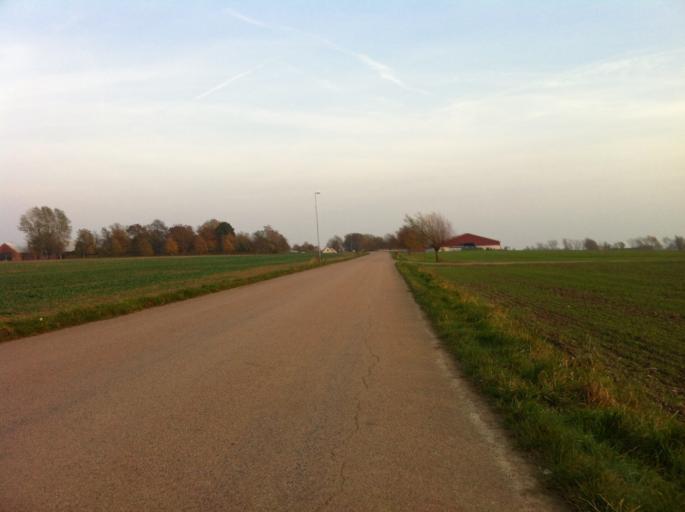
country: SE
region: Skane
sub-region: Svalovs Kommun
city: Teckomatorp
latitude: 55.8767
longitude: 13.0211
